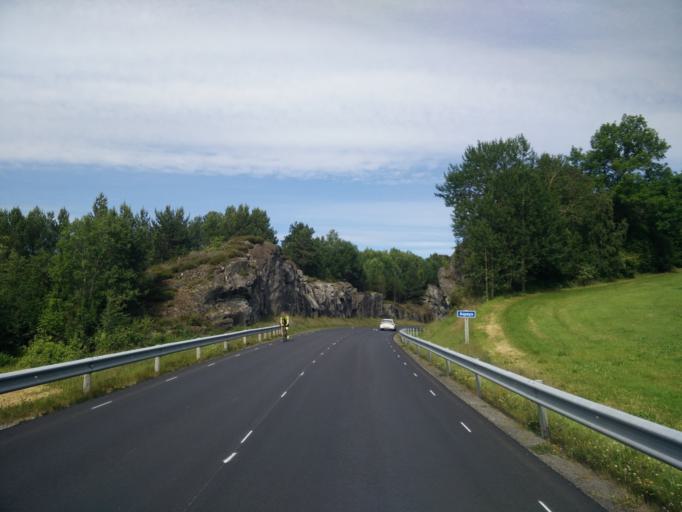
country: NO
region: More og Romsdal
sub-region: Kristiansund
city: Rensvik
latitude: 62.9907
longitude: 7.8831
